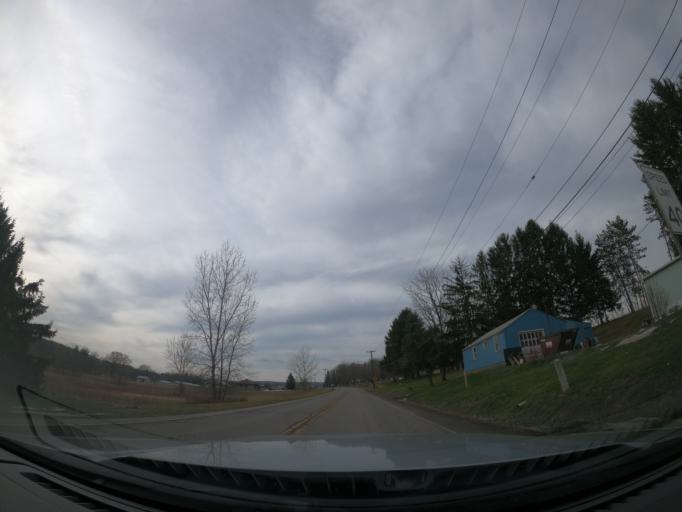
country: US
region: New York
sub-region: Yates County
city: Dundee
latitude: 42.5263
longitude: -76.9835
